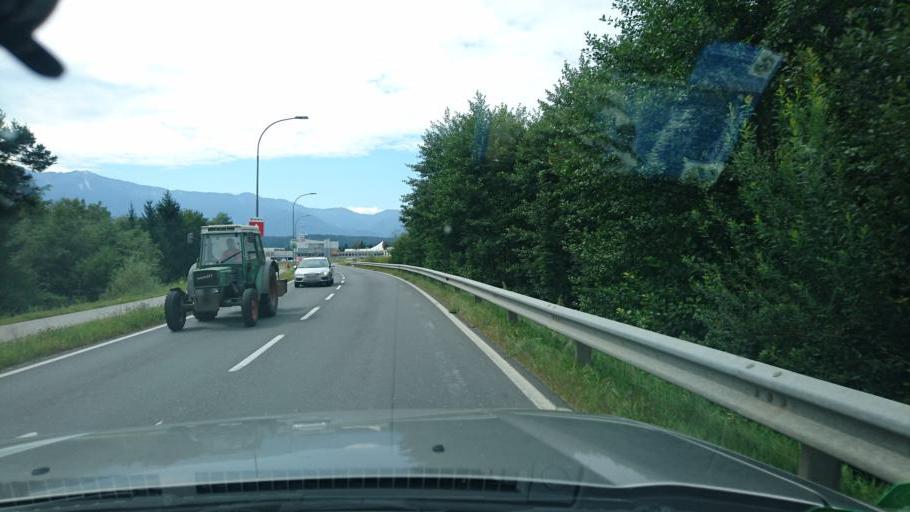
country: AT
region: Carinthia
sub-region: Villach Stadt
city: Villach
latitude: 46.6073
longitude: 13.8765
